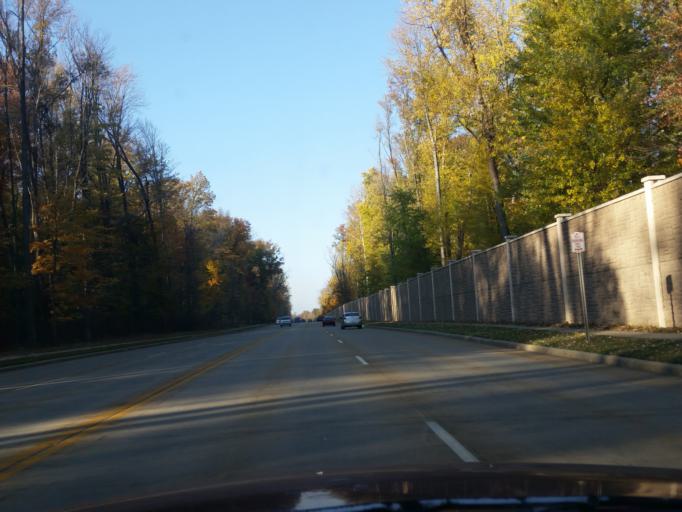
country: US
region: Ohio
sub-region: Cuyahoga County
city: North Olmsted
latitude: 41.4145
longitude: -81.9436
